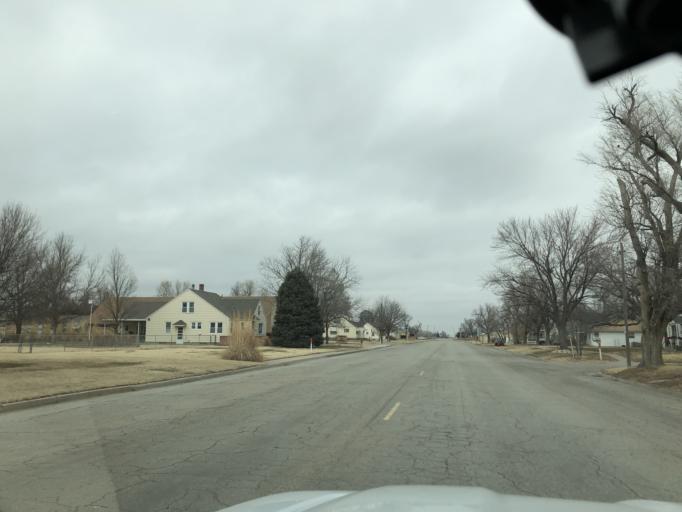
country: US
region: Kansas
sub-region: Stafford County
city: Stafford
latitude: 37.9650
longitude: -98.6005
